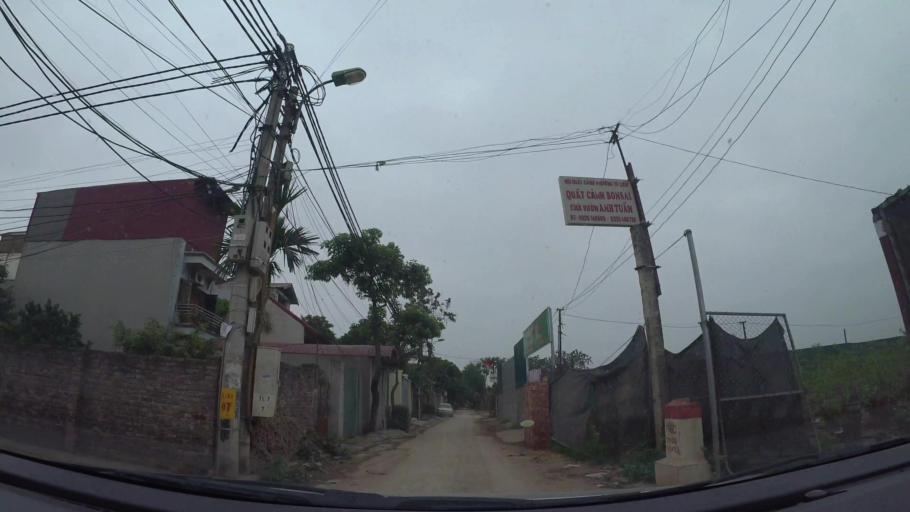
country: VN
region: Ha Noi
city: Tay Ho
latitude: 21.0629
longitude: 105.8384
